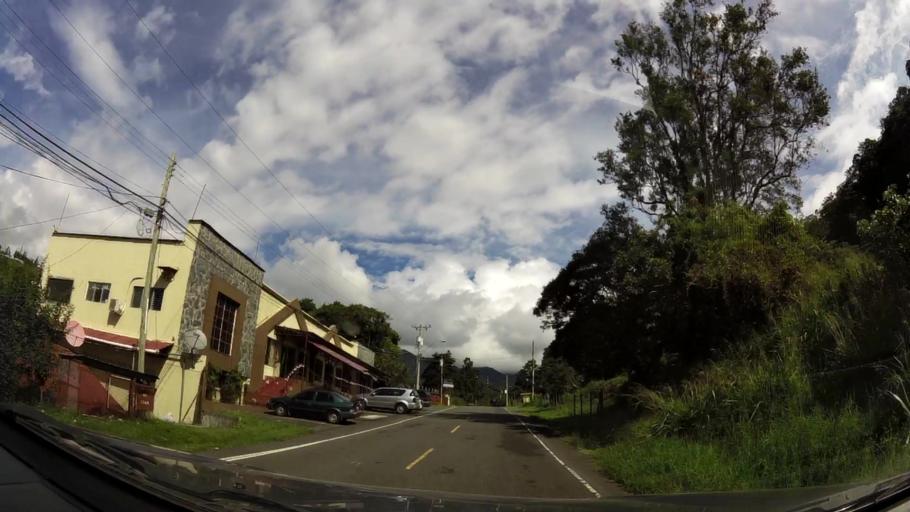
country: PA
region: Chiriqui
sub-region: Distrito Boquete
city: Boquete
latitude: 8.7788
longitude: -82.4299
